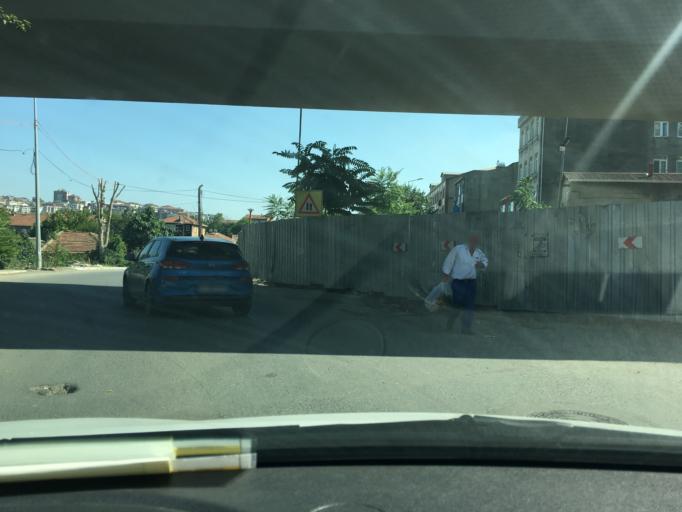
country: TR
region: Istanbul
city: Sisli
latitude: 41.0794
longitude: 28.9475
